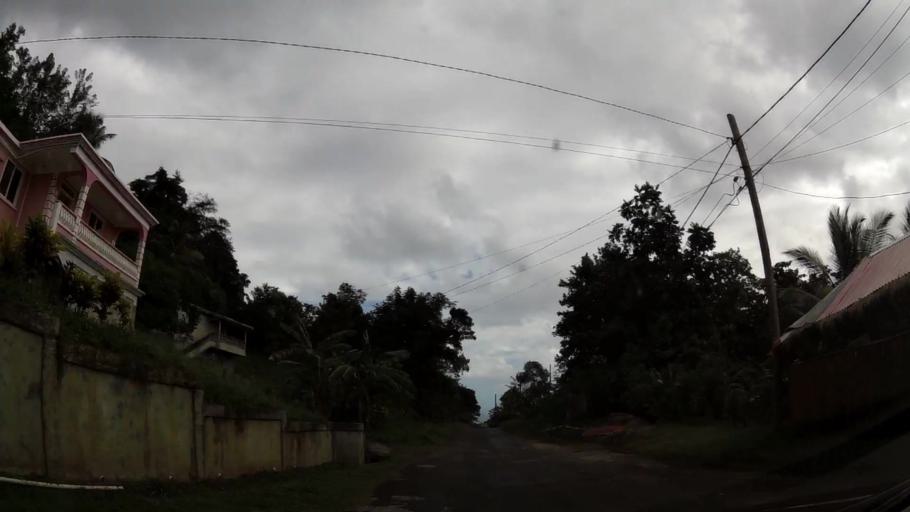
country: DM
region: Saint David
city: Castle Bruce
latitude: 15.4467
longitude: -61.2583
